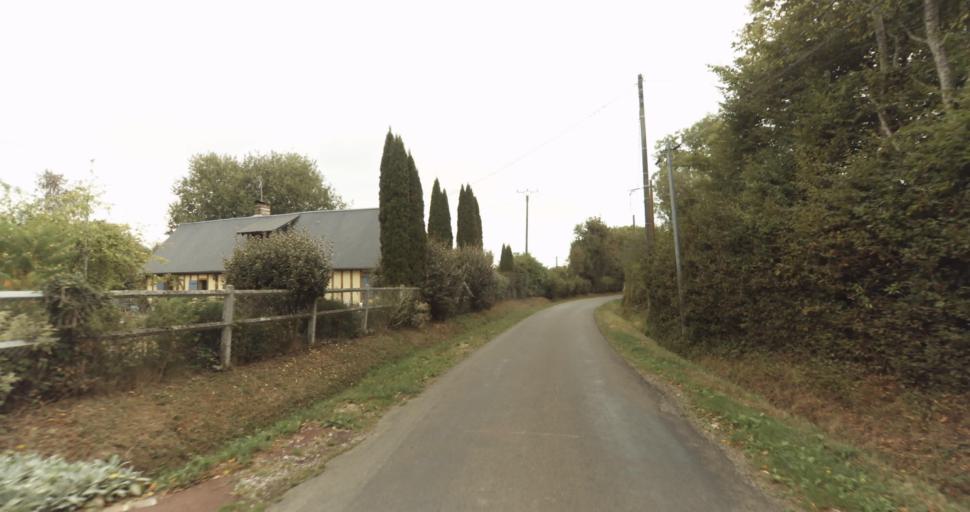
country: FR
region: Lower Normandy
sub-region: Departement de l'Orne
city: Gace
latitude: 48.8530
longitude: 0.3211
